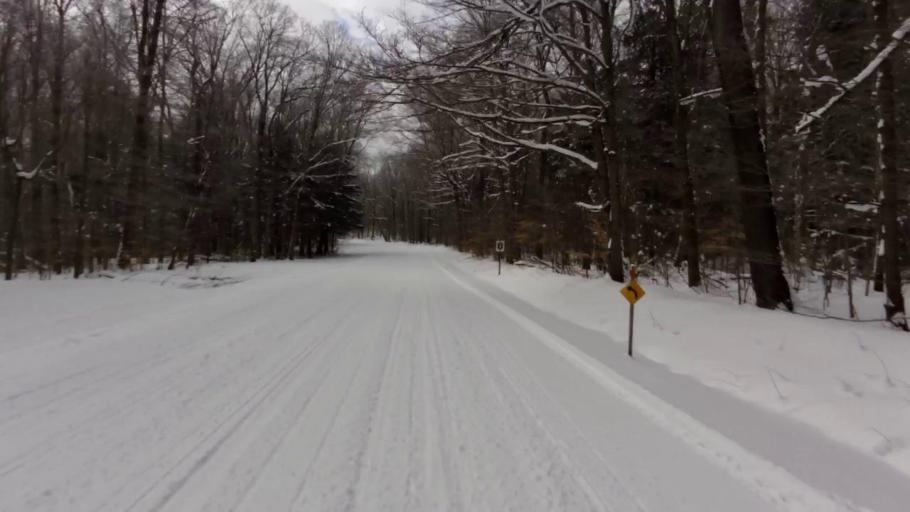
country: US
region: New York
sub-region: Cattaraugus County
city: Salamanca
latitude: 42.0497
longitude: -78.7718
